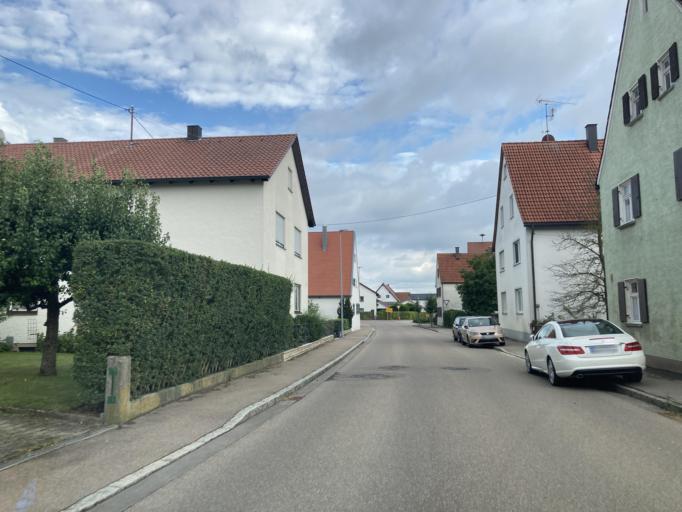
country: DE
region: Bavaria
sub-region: Swabia
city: Medlingen
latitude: 48.5685
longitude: 10.3172
